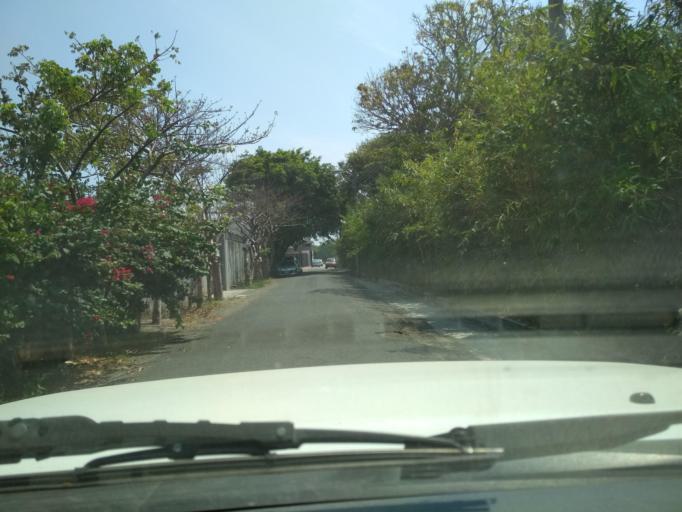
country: MX
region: Veracruz
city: Boca del Rio
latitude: 19.0953
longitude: -96.1214
